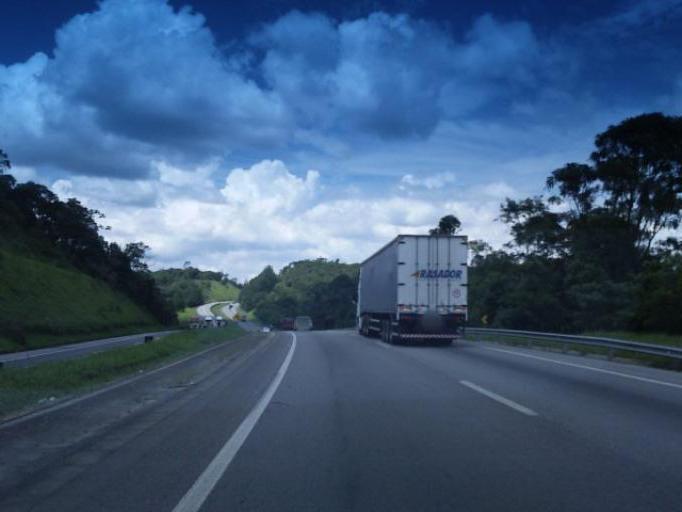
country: BR
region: Sao Paulo
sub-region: Juquitiba
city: Juquitiba
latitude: -23.9600
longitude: -47.1188
